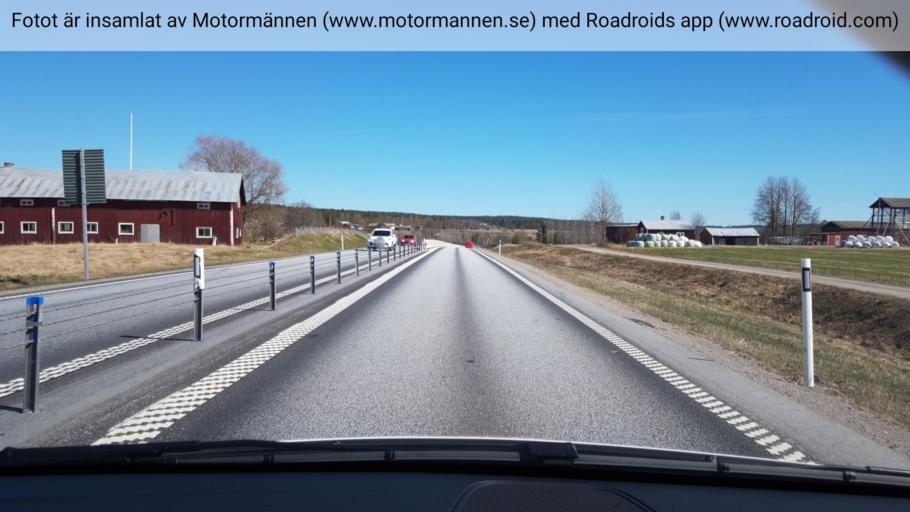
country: SE
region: Vaesterbotten
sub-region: Umea Kommun
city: Roback
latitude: 63.8869
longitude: 20.0176
